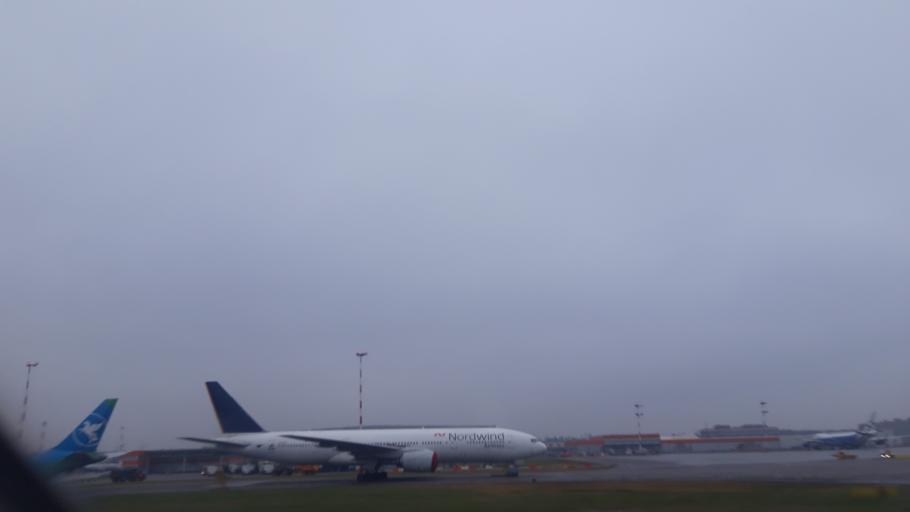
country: RU
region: Moskovskaya
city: Lobnya
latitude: 55.9775
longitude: 37.4266
